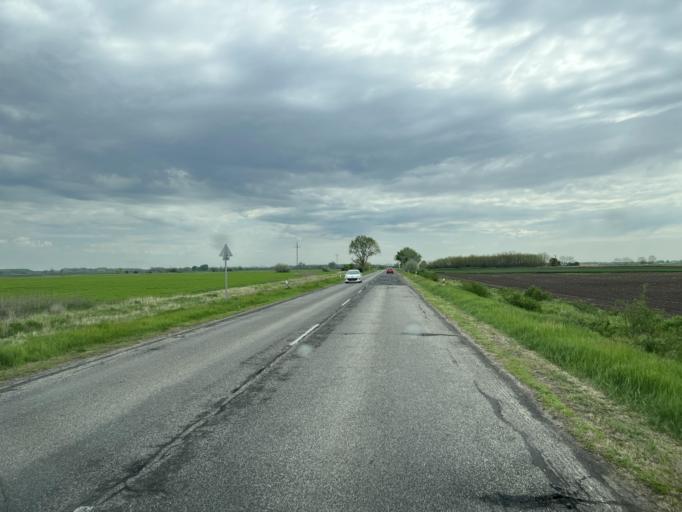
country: HU
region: Pest
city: Abony
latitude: 47.1864
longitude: 19.9419
